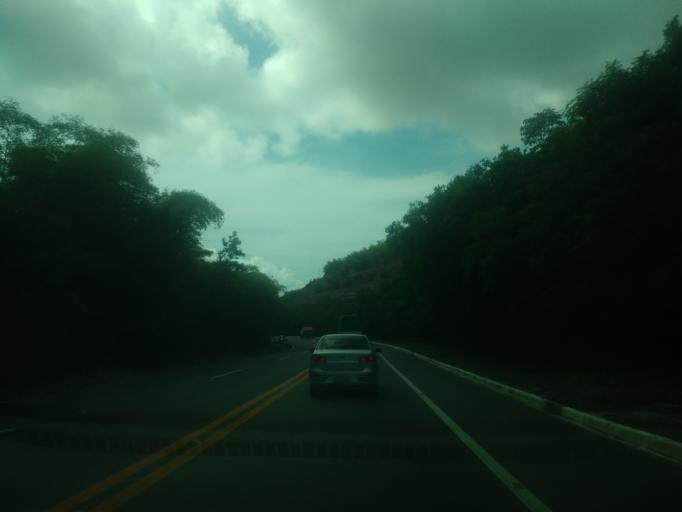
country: BR
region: Alagoas
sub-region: Marechal Deodoro
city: Marechal Deodoro
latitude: -9.6869
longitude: -35.8197
